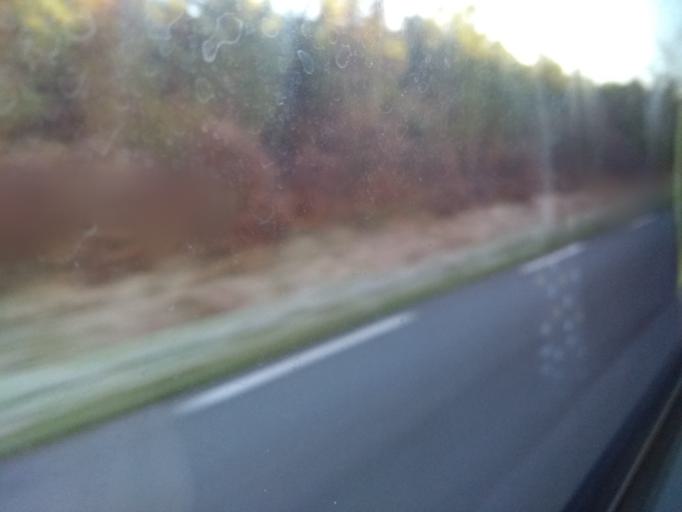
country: FR
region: Aquitaine
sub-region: Departement de la Gironde
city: Le Barp
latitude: 44.6189
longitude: -0.7624
